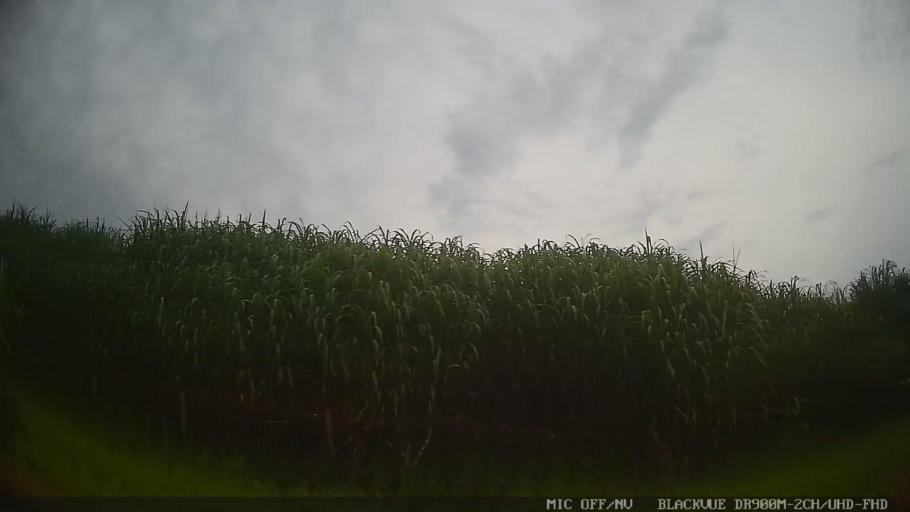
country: BR
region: Sao Paulo
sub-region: Suzano
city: Suzano
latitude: -23.6609
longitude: -46.2775
